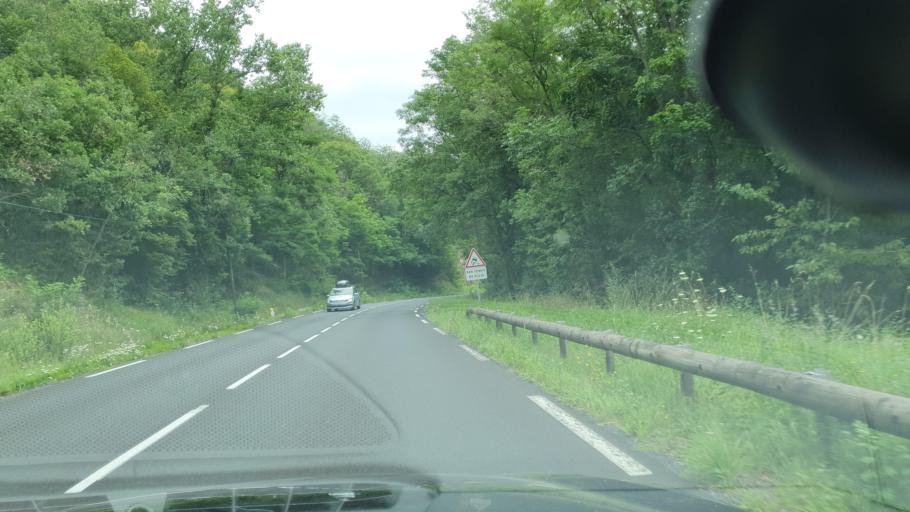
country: FR
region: Auvergne
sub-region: Departement du Puy-de-Dome
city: Champeix
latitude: 45.5735
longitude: 3.0606
